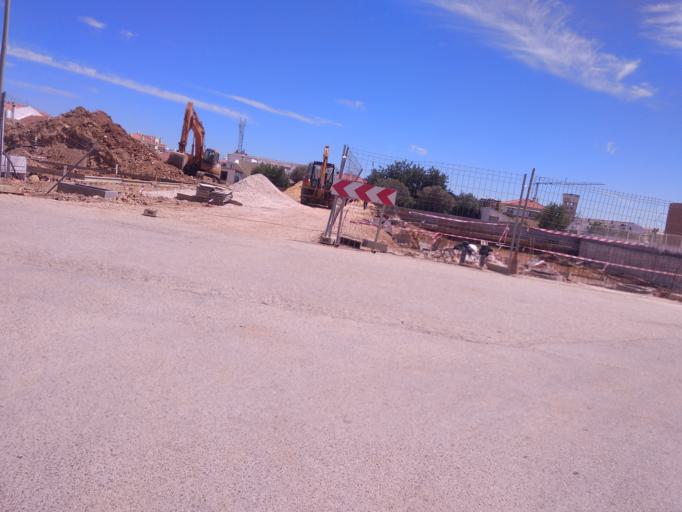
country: PT
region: Faro
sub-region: Sao Bras de Alportel
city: Sao Bras de Alportel
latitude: 37.1541
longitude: -7.8841
